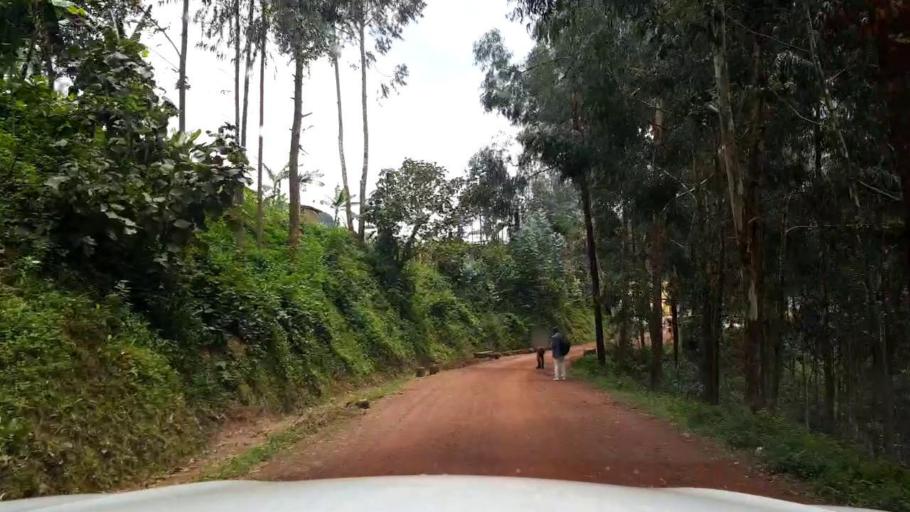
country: UG
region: Western Region
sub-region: Kabale District
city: Kabale
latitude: -1.4322
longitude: 29.8693
